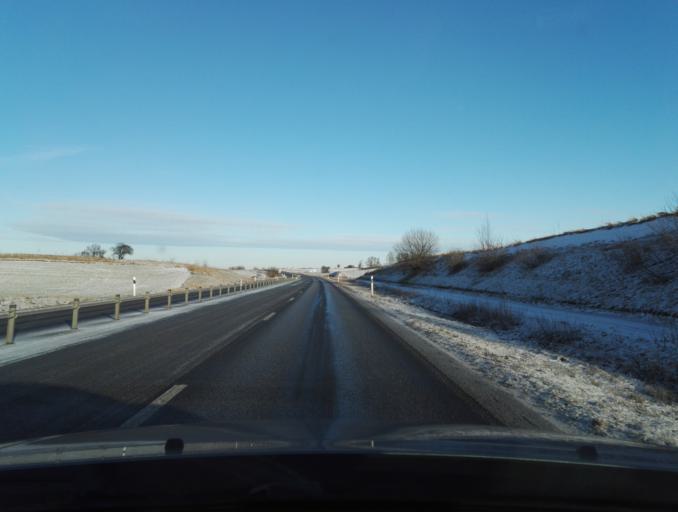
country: SE
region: Skane
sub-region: Svedala Kommun
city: Svedala
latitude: 55.4872
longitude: 13.2332
